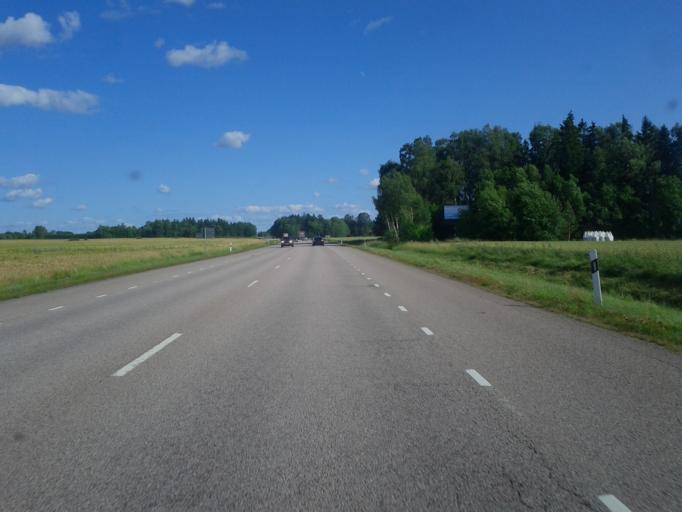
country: SE
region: Uppsala
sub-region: Enkopings Kommun
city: Enkoping
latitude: 59.6801
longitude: 17.0445
